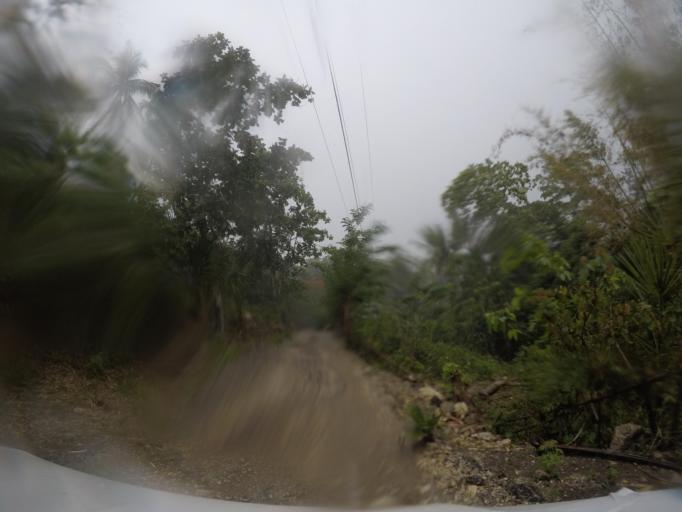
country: TL
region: Baucau
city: Venilale
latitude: -8.6344
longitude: 126.4391
